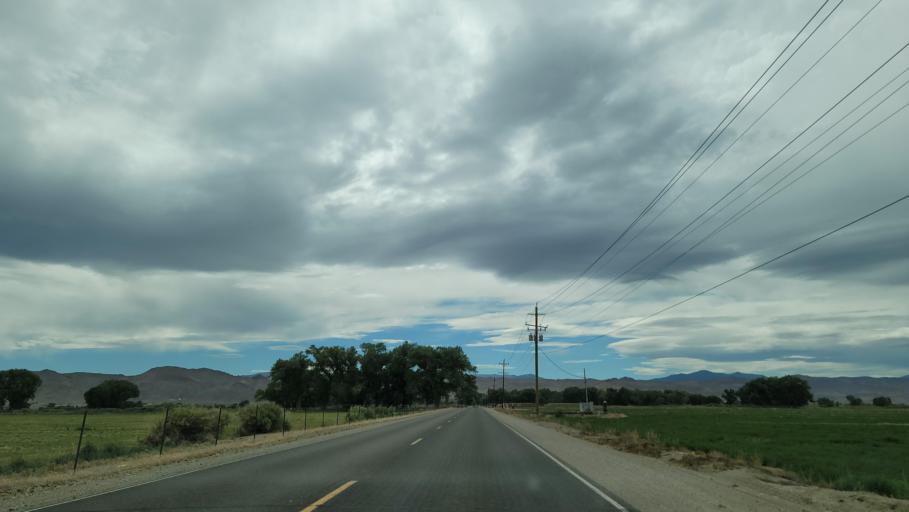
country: US
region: Nevada
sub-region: Lyon County
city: Yerington
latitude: 39.0481
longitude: -119.1672
